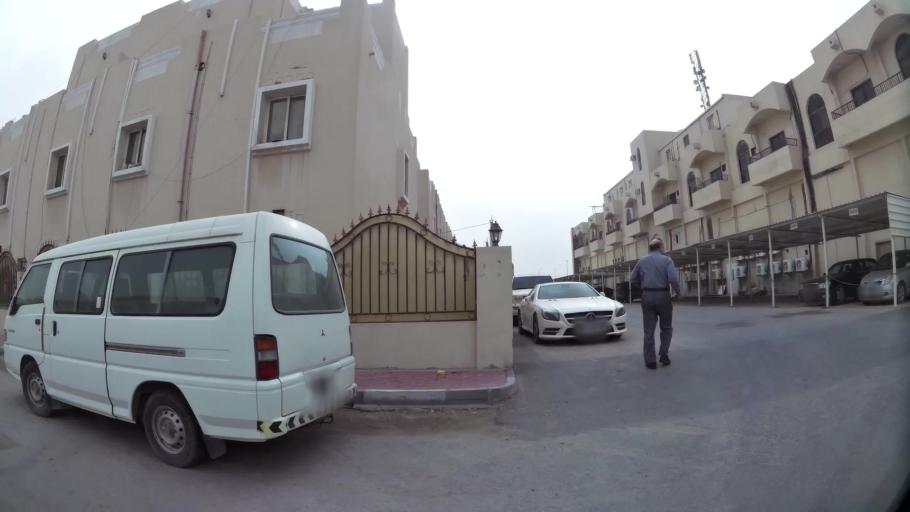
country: QA
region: Baladiyat ad Dawhah
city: Doha
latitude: 25.2570
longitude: 51.4868
